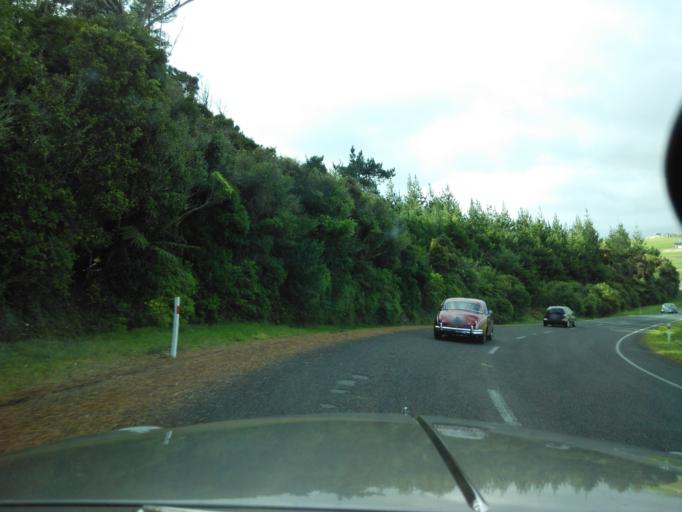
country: NZ
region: Auckland
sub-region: Auckland
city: Pukekohe East
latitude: -37.1450
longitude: 175.0183
